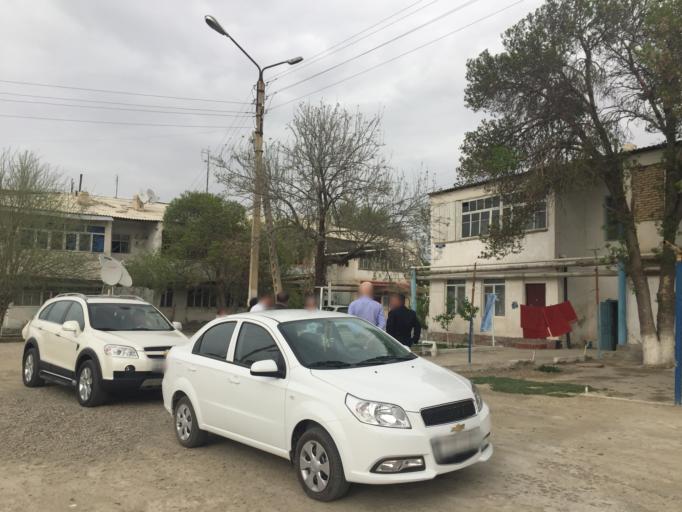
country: UZ
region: Bukhara
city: Kogon
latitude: 39.7381
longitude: 64.5574
